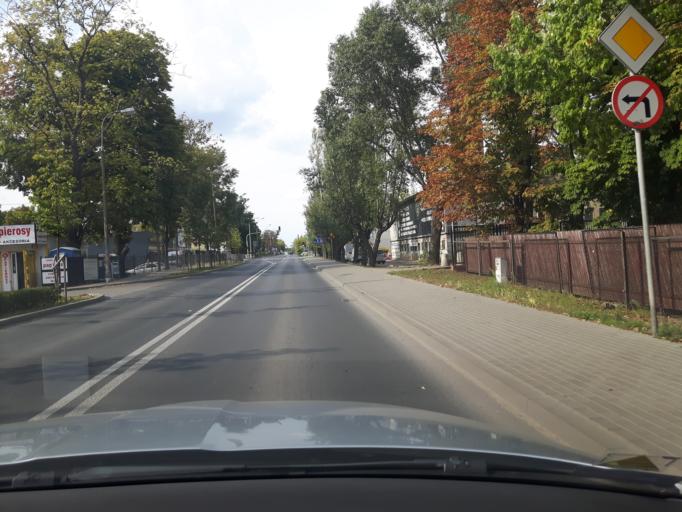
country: PL
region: Masovian Voivodeship
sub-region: Powiat piaseczynski
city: Piaseczno
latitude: 52.0756
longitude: 21.0224
